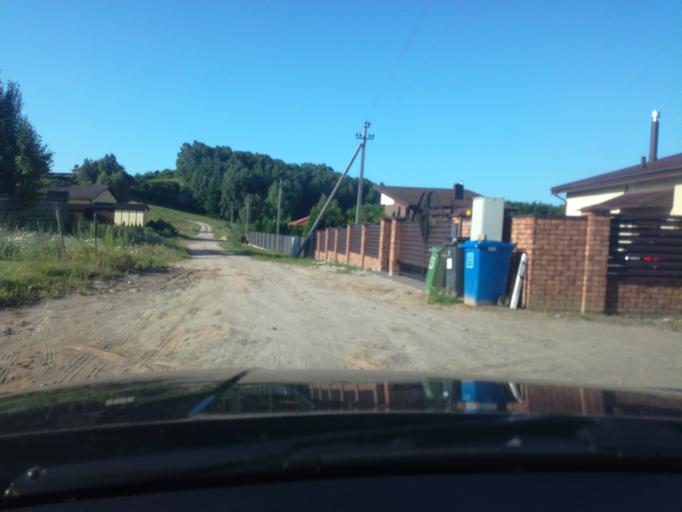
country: LT
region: Alytaus apskritis
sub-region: Alytus
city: Alytus
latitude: 54.4035
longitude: 23.9961
